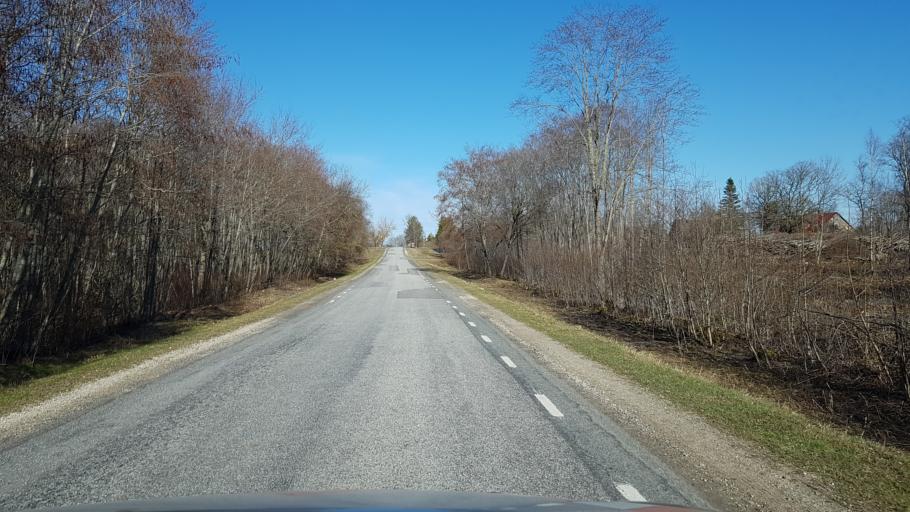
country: EE
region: Laeaene-Virumaa
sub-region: Kadrina vald
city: Kadrina
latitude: 59.3514
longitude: 26.1133
